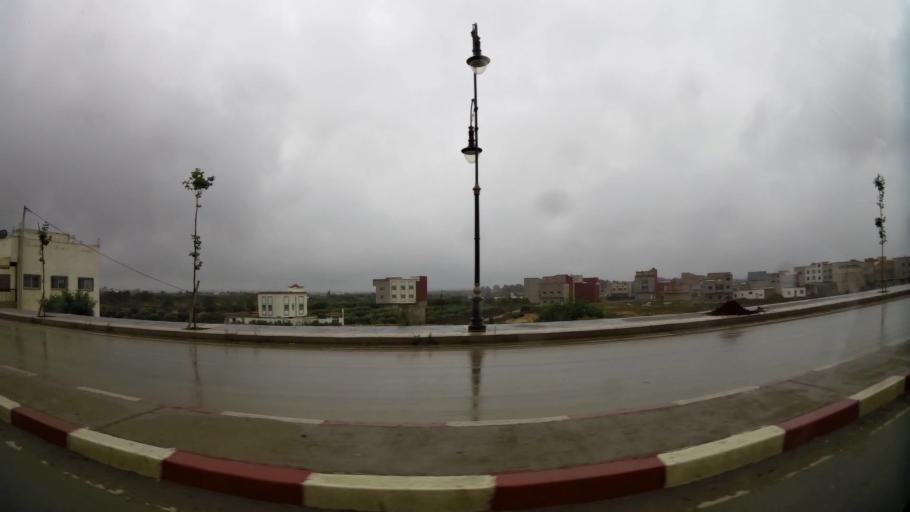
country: MA
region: Taza-Al Hoceima-Taounate
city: Imzourene
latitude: 35.1551
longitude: -3.8460
